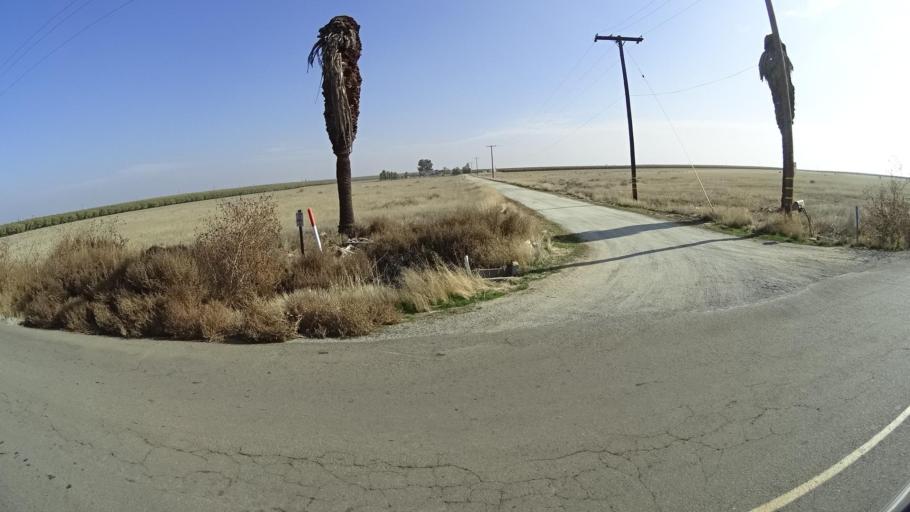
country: US
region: California
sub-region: Kern County
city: McFarland
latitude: 35.6639
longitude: -119.1693
